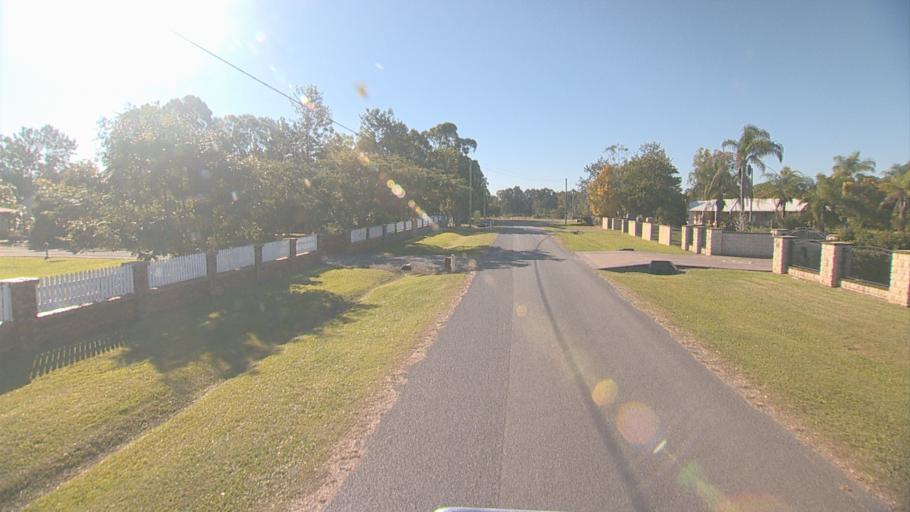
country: AU
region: Queensland
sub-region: Logan
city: Logan Reserve
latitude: -27.7389
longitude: 153.1134
